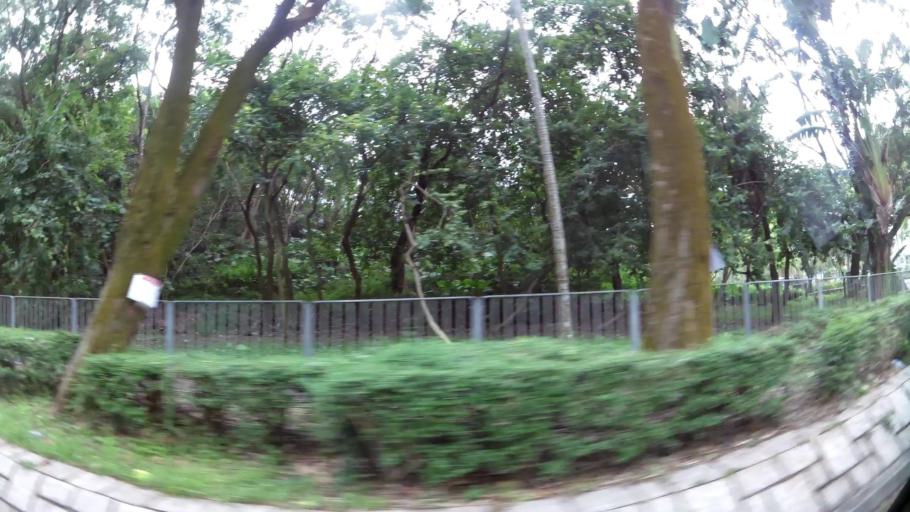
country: HK
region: Tai Po
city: Tai Po
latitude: 22.4413
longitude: 114.1649
